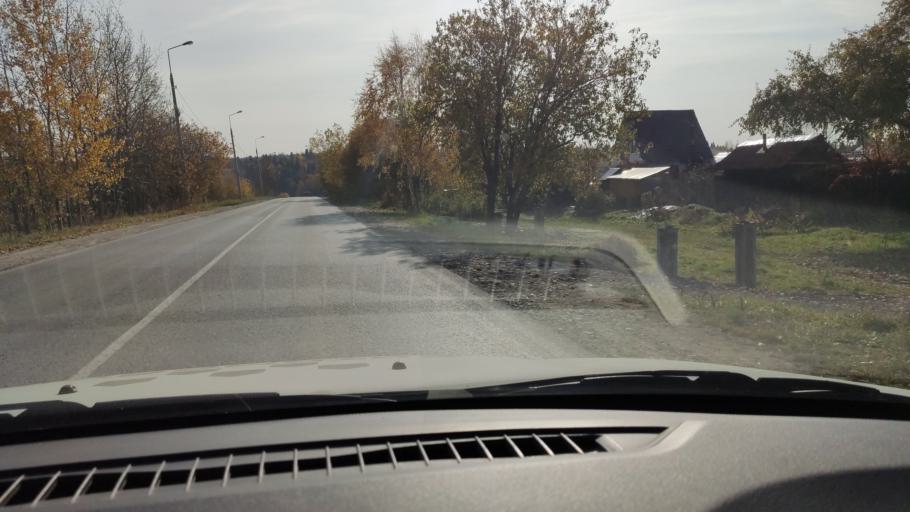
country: RU
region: Perm
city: Novyye Lyady
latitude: 58.0430
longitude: 56.5957
